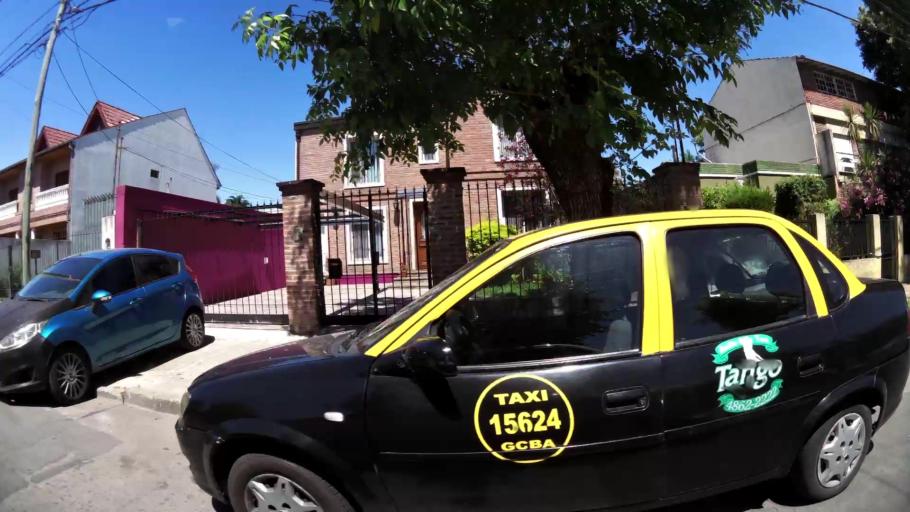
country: AR
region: Buenos Aires
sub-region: Partido de General San Martin
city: General San Martin
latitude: -34.5253
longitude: -58.5521
